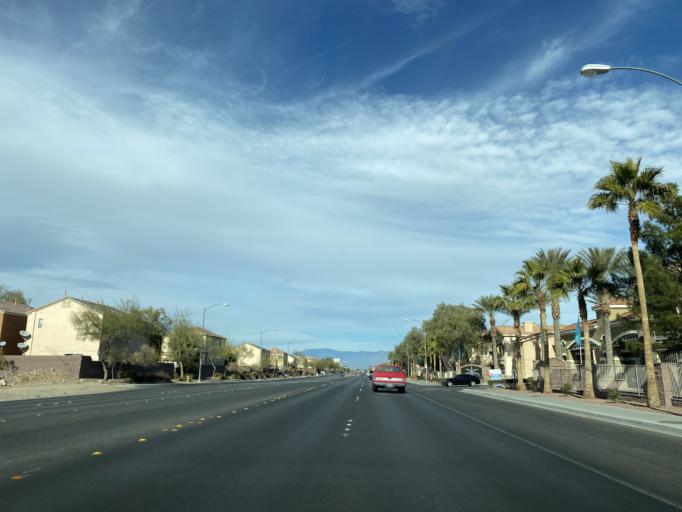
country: US
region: Nevada
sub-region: Clark County
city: Enterprise
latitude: 36.0505
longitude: -115.2252
